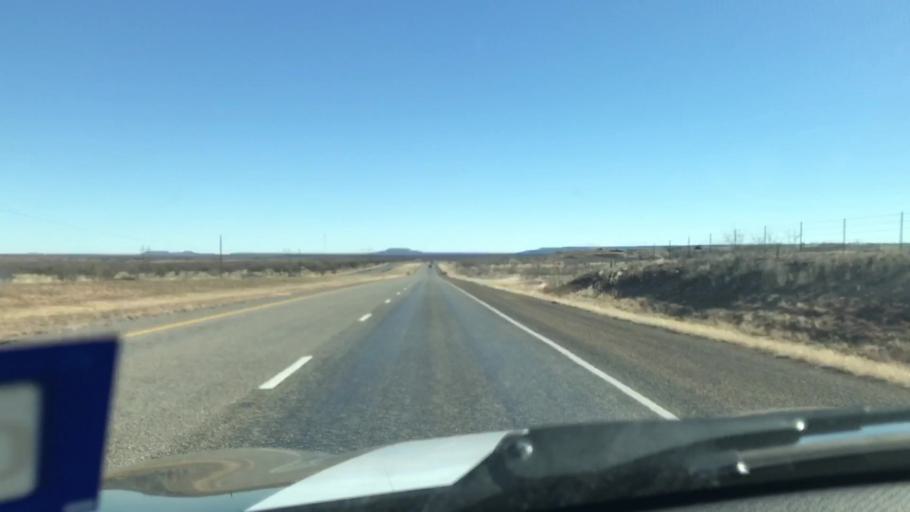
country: US
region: Texas
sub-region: Garza County
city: Post
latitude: 33.0654
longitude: -101.2244
